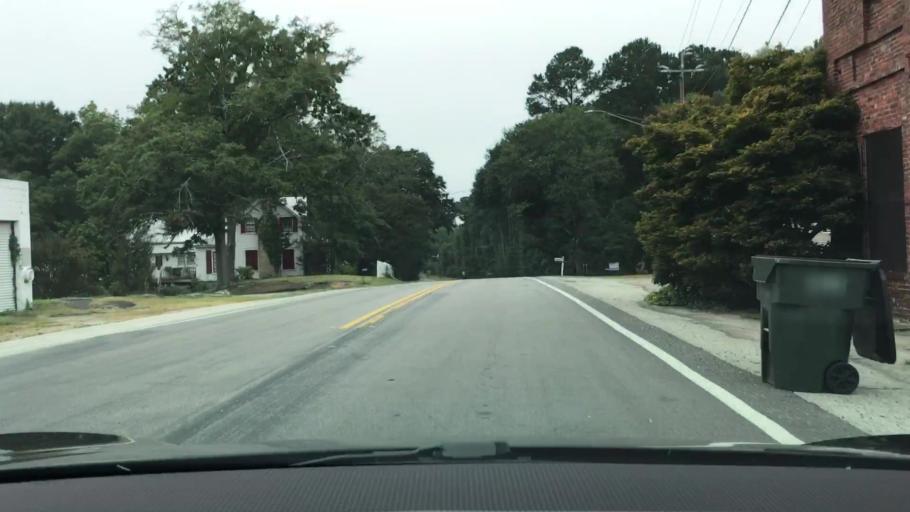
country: US
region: Georgia
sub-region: Greene County
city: Union Point
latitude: 33.5366
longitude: -83.0815
